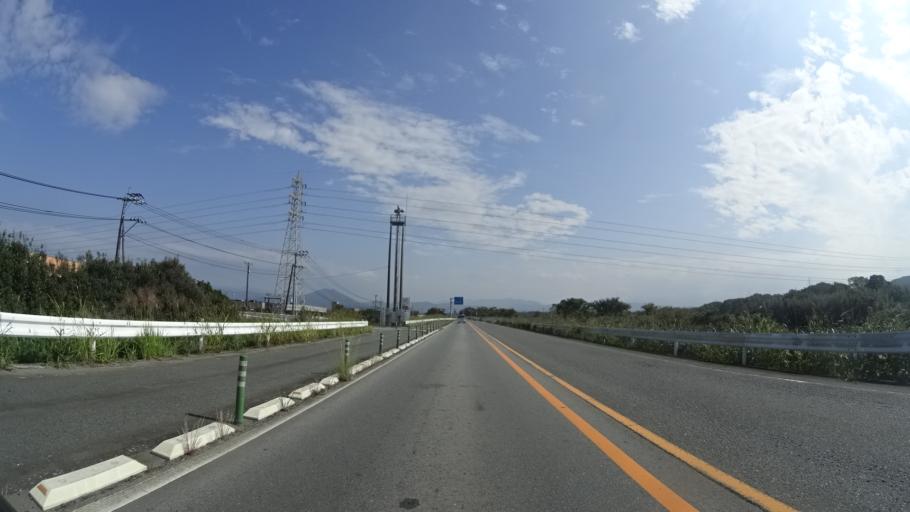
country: JP
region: Kumamoto
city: Kumamoto
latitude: 32.7360
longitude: 130.7473
